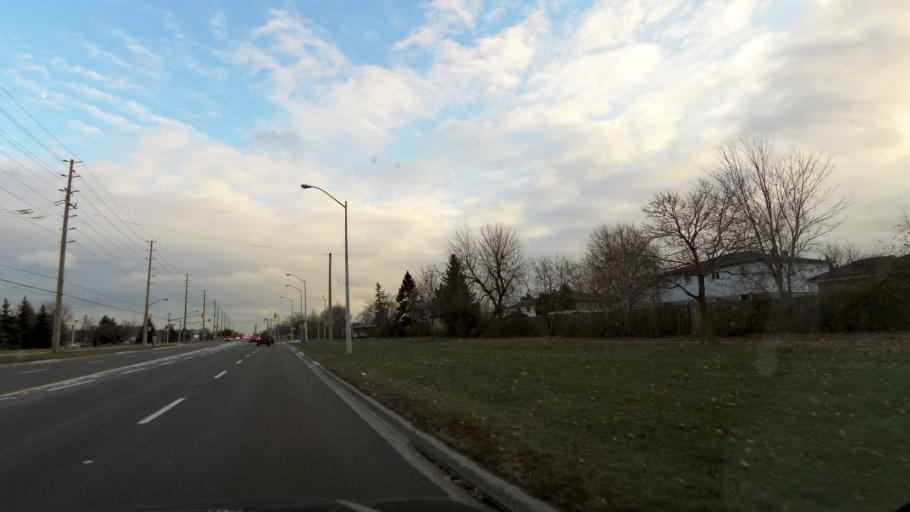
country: CA
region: Ontario
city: Brampton
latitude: 43.7370
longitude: -79.7108
